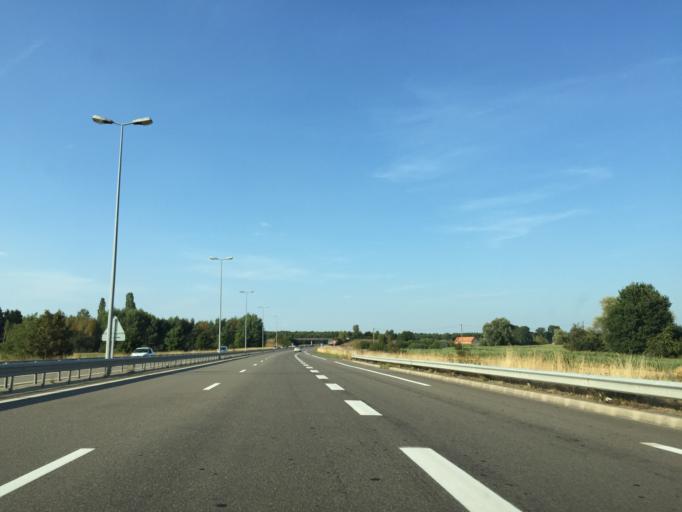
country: FR
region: Alsace
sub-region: Departement du Bas-Rhin
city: Haguenau
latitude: 48.8306
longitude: 7.7622
